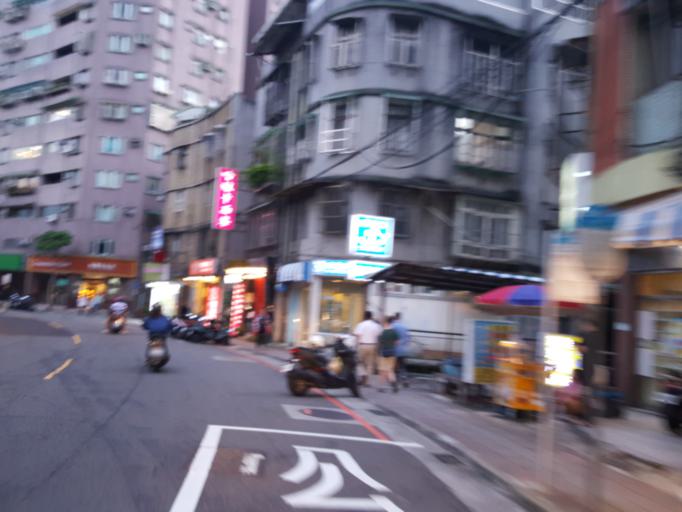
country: TW
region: Taipei
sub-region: Taipei
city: Banqiao
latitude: 25.0002
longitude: 121.5109
